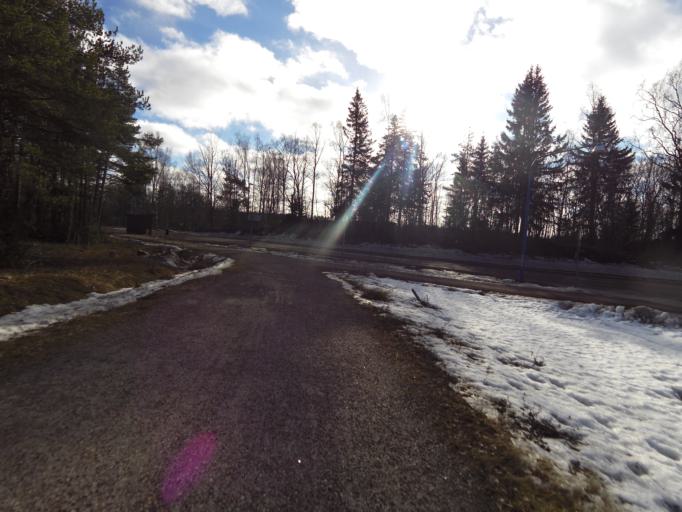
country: SE
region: Uppsala
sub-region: Alvkarleby Kommun
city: Skutskaer
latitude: 60.6491
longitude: 17.3642
